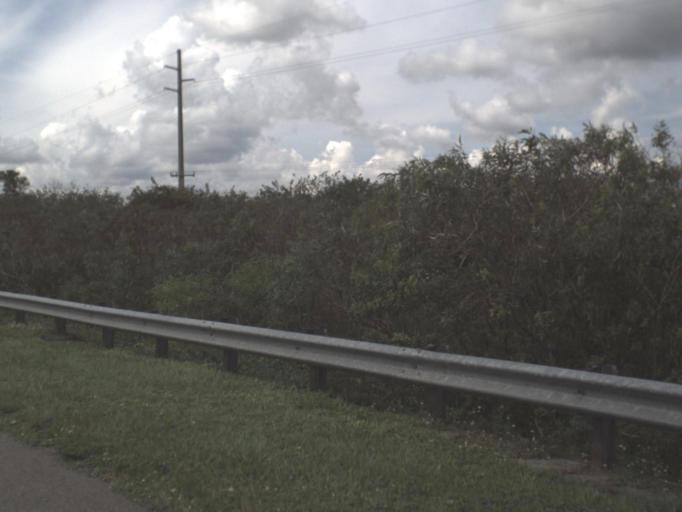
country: US
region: Florida
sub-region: Glades County
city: Buckhead Ridge
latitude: 27.2143
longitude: -81.1116
